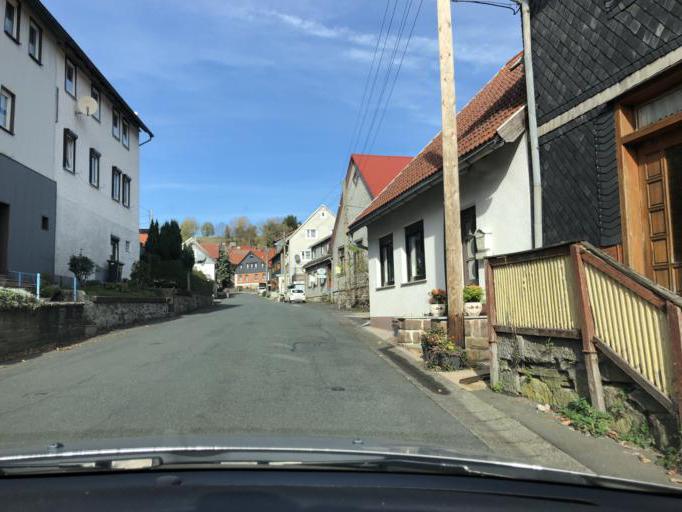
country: DE
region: Thuringia
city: Masserberg
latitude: 50.5033
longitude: 10.9249
